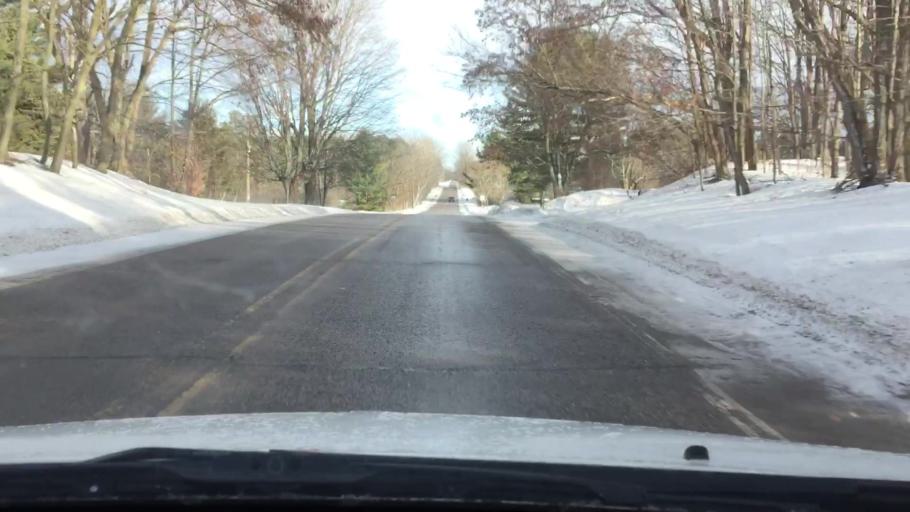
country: US
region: Michigan
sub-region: Kalkaska County
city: Kalkaska
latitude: 44.6412
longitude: -85.2715
